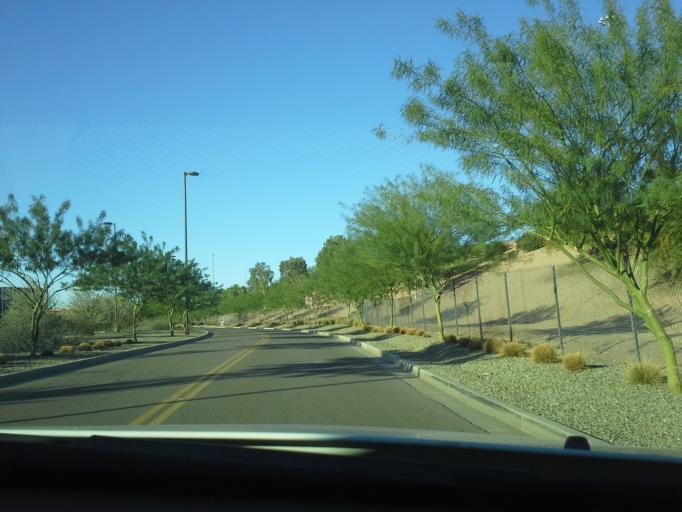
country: US
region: Arizona
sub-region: Maricopa County
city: Tempe
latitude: 33.4331
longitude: -111.8852
